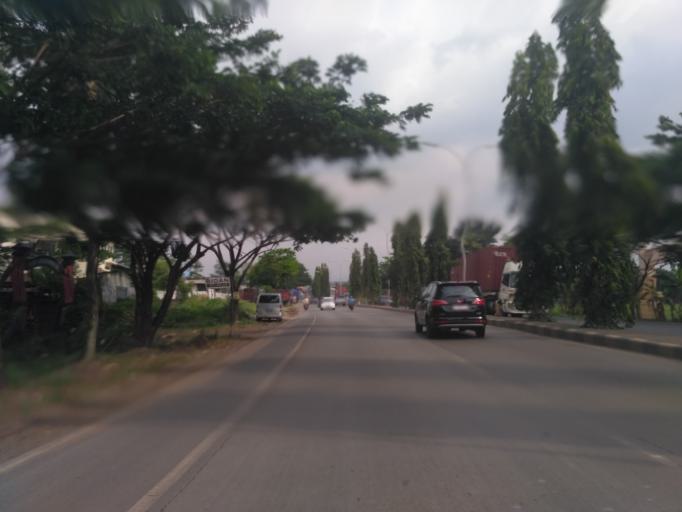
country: ID
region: Central Java
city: Semarang
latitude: -6.9753
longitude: 110.3876
